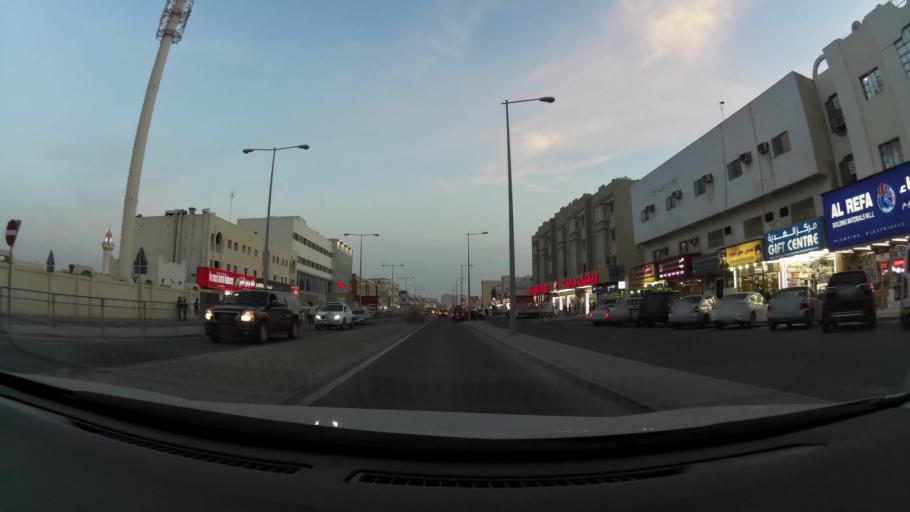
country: QA
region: Al Wakrah
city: Al Wakrah
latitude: 25.1588
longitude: 51.5991
